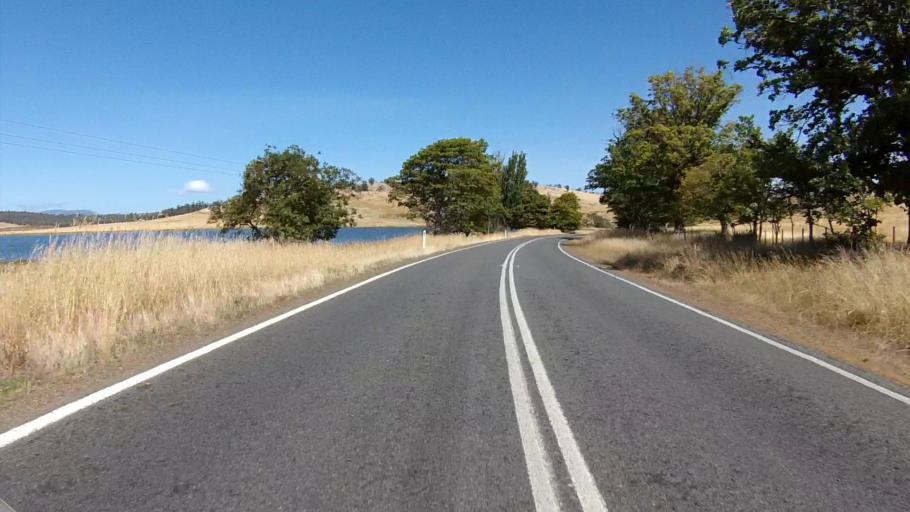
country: AU
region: Tasmania
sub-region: Sorell
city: Sorell
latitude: -42.4872
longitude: 147.9347
